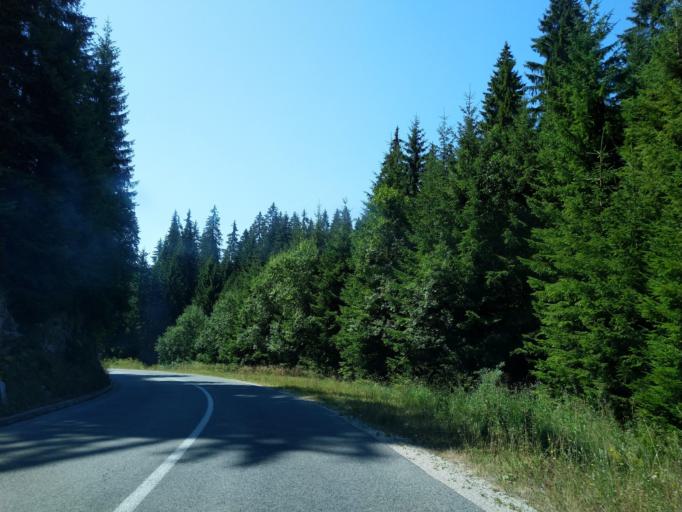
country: RS
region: Central Serbia
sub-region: Zlatiborski Okrug
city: Nova Varos
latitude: 43.3977
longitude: 19.8435
